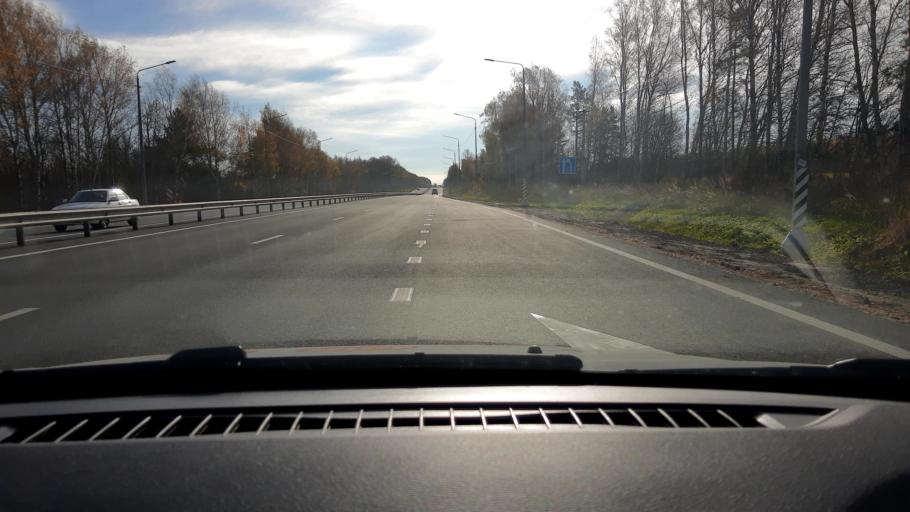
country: RU
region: Nizjnij Novgorod
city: Burevestnik
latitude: 56.0627
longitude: 43.9420
